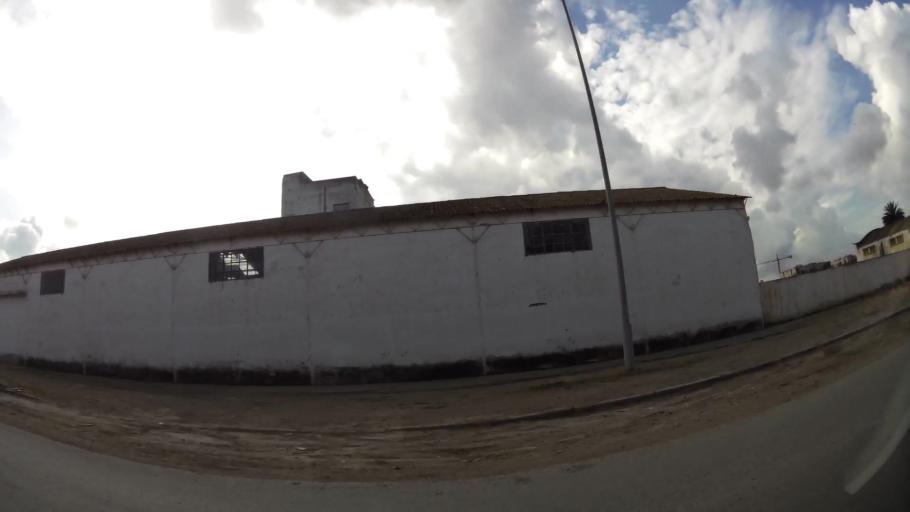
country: MA
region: Gharb-Chrarda-Beni Hssen
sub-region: Kenitra Province
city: Kenitra
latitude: 34.2767
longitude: -6.5602
